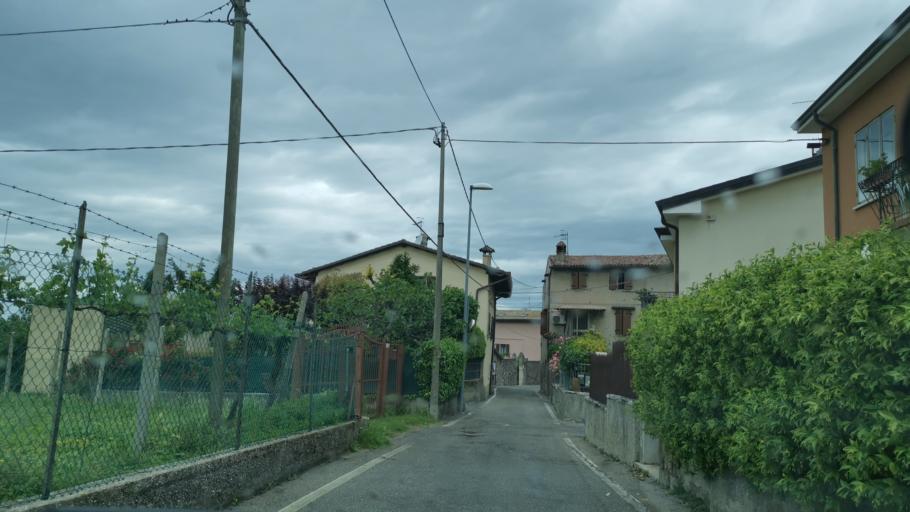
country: IT
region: Veneto
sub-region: Provincia di Verona
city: Bardolino
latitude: 45.5403
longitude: 10.7461
